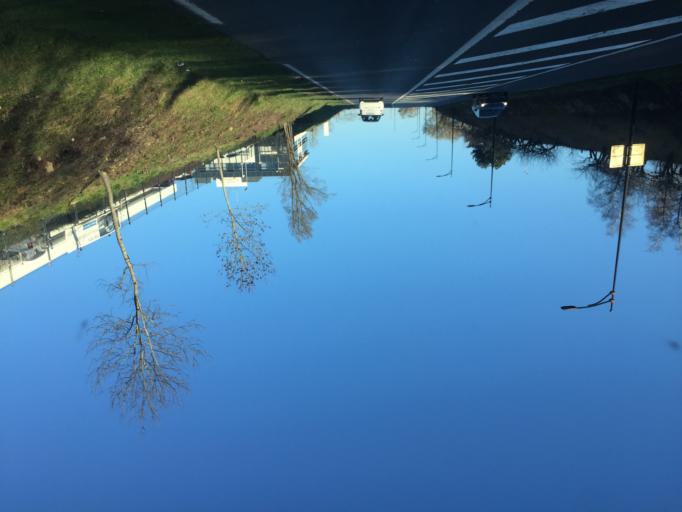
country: FR
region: Bourgogne
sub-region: Departement de l'Yonne
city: Auxerre
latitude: 47.8111
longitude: 3.5630
